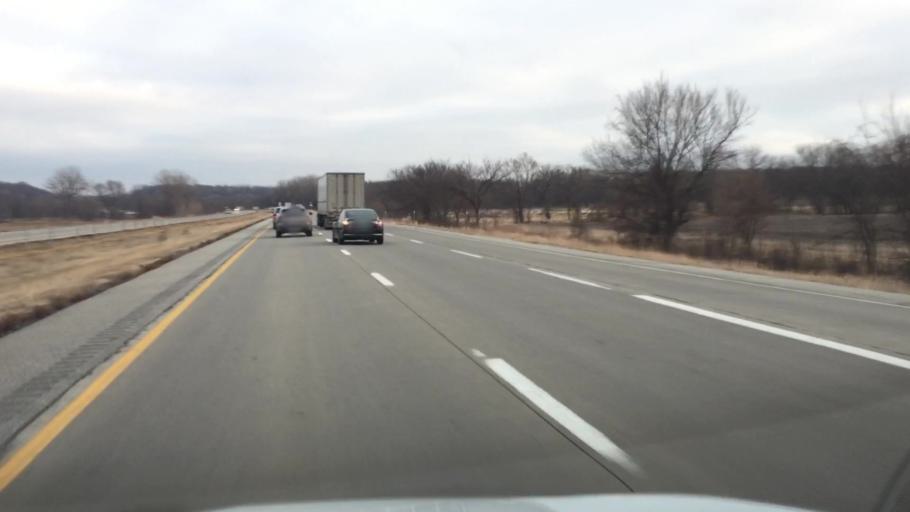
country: US
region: Iowa
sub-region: Jasper County
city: Colfax
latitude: 41.6888
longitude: -93.1755
